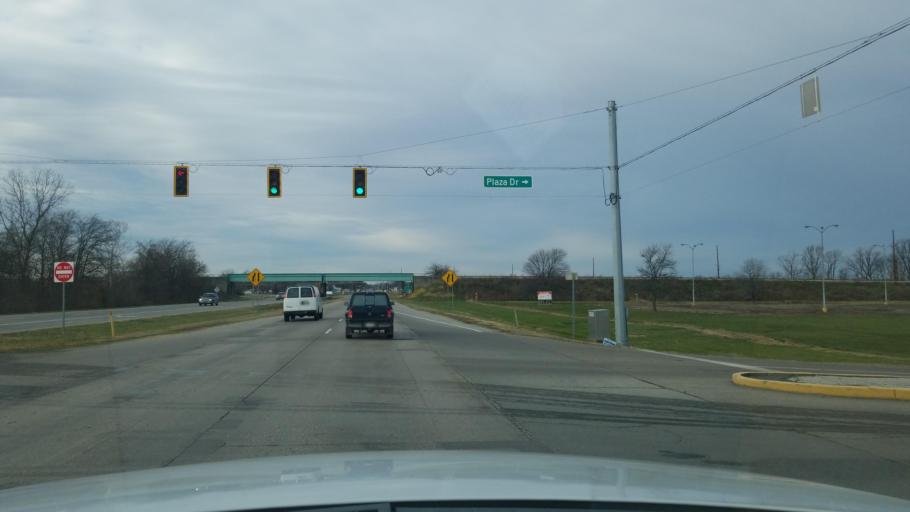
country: US
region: Indiana
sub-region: Posey County
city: Mount Vernon
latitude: 37.9389
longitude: -87.8699
